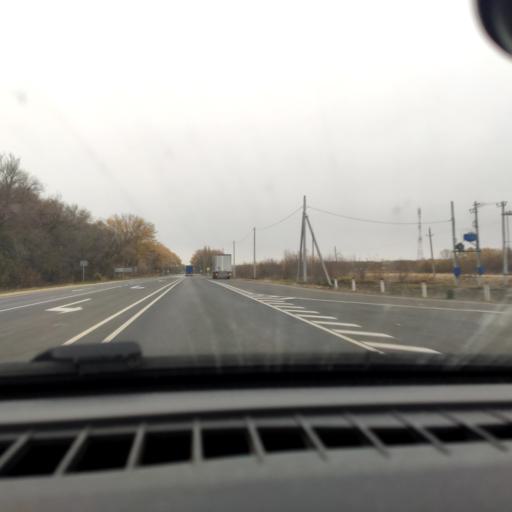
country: RU
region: Voronezj
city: Uryv-Pokrovka
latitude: 51.1706
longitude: 39.0750
